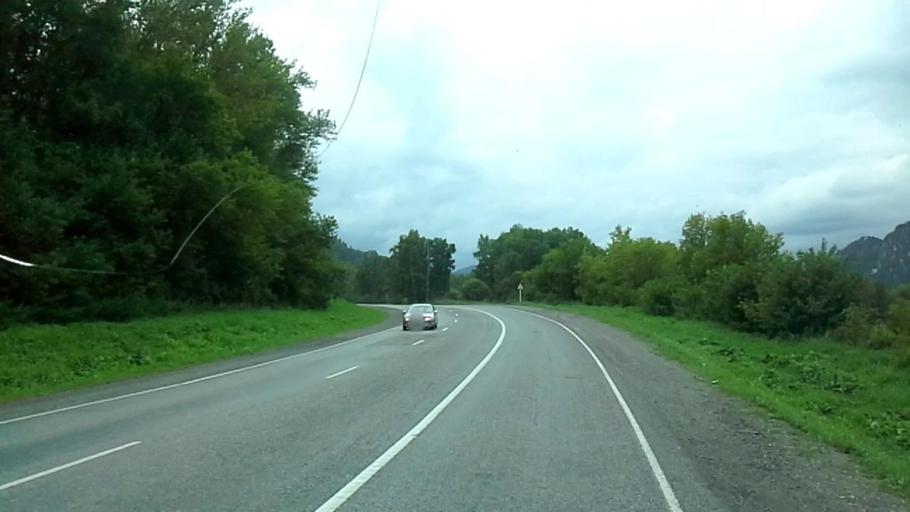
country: RU
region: Altay
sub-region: Mayminskiy Rayon
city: Manzherok
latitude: 51.8627
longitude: 85.7616
